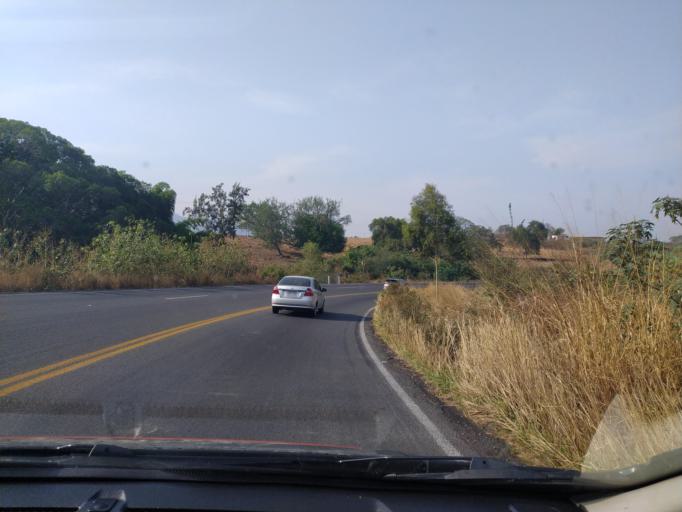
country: MX
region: Jalisco
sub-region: Acatlan de Juarez
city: Villa de los Ninos
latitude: 20.4175
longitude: -103.5790
